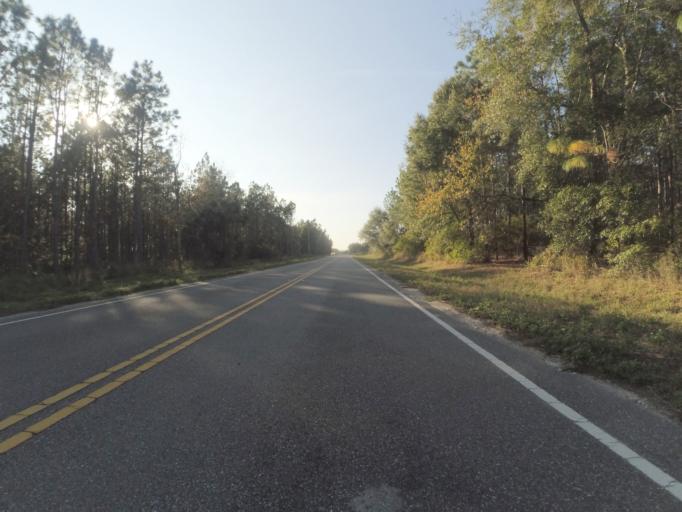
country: US
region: Florida
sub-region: Lake County
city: Umatilla
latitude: 28.9604
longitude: -81.6628
